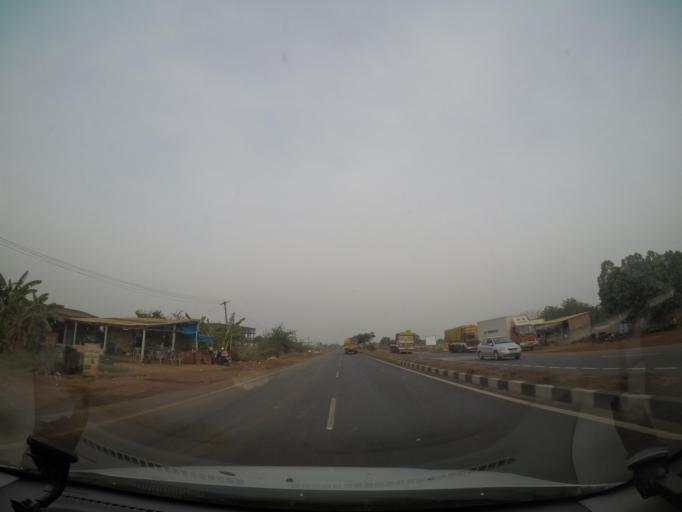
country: IN
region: Andhra Pradesh
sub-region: West Godavari
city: Eluru
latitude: 16.6323
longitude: 80.9550
